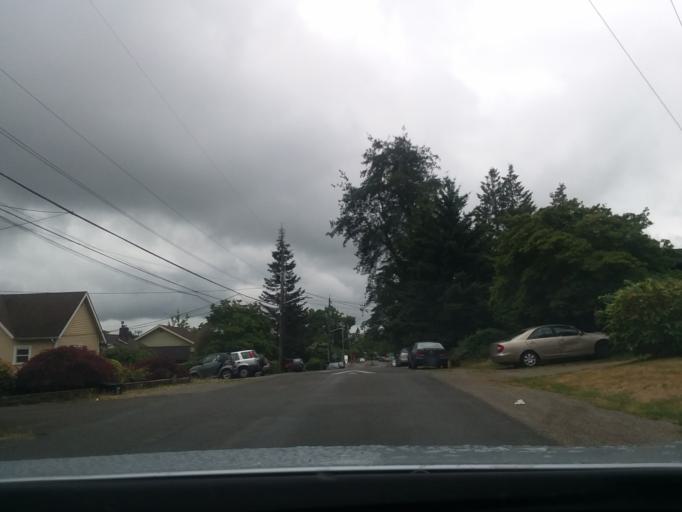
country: US
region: Washington
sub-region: King County
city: Lake Forest Park
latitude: 47.7224
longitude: -122.2991
